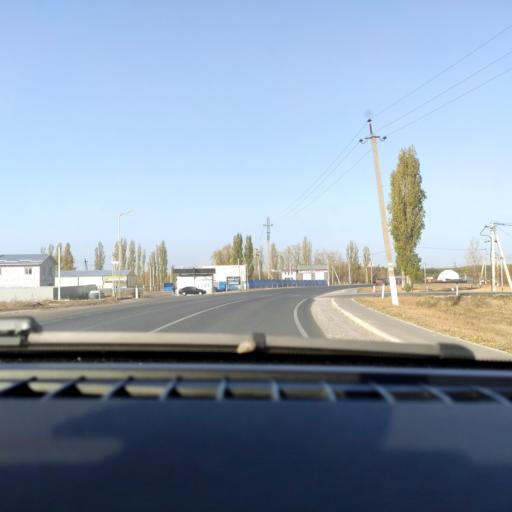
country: RU
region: Voronezj
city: Novaya Usman'
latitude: 51.6591
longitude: 39.4019
